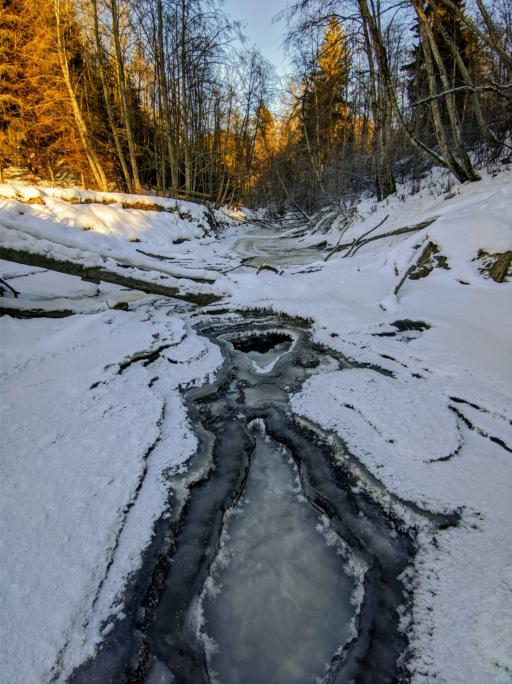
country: NO
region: Akershus
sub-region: Nannestad
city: Teigebyen
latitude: 60.1656
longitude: 11.0582
